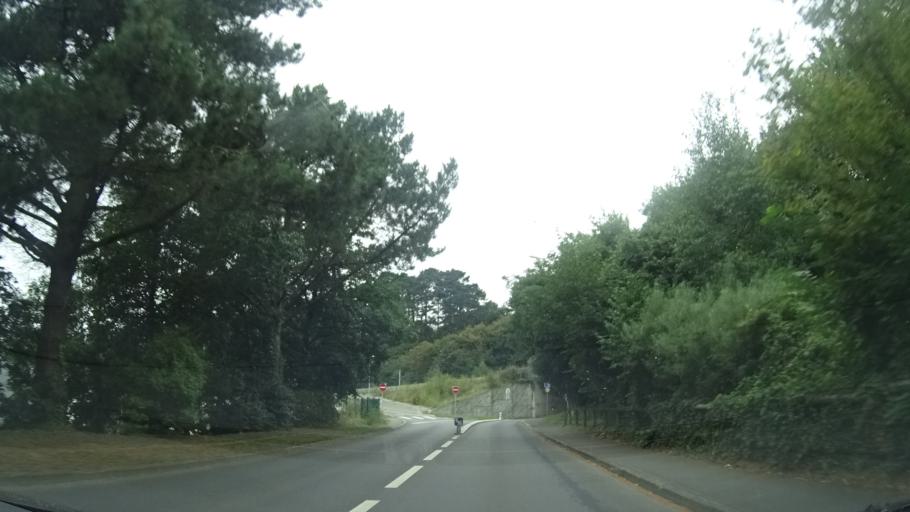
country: FR
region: Brittany
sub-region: Departement du Finistere
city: Brest
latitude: 48.3928
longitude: -4.4479
